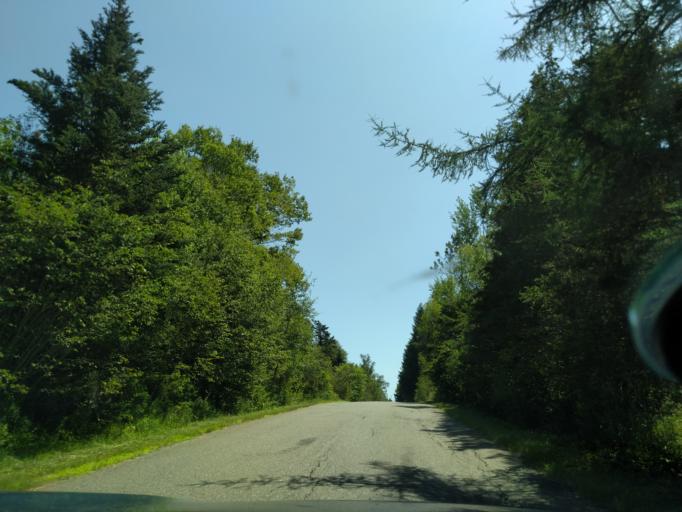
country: US
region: Maine
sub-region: Washington County
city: Eastport
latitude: 44.8340
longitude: -67.0089
